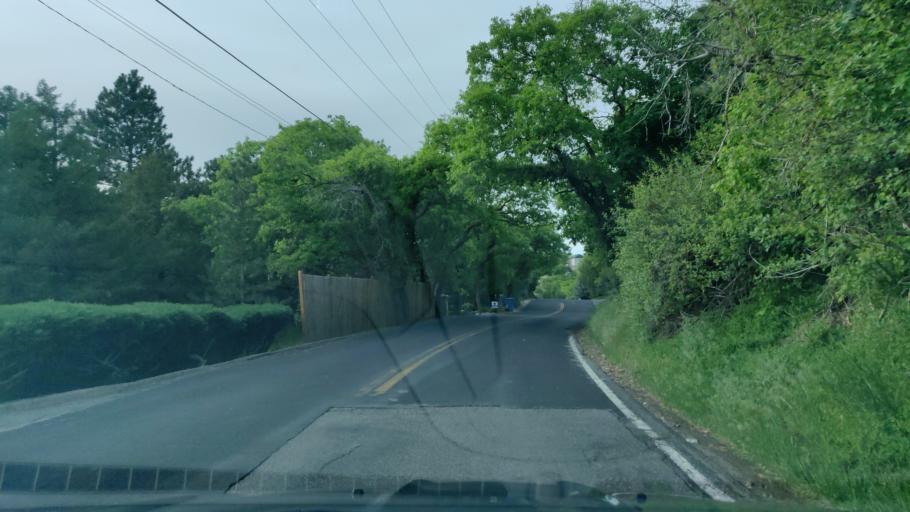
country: US
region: Utah
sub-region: Salt Lake County
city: Granite
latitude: 40.5944
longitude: -111.8008
